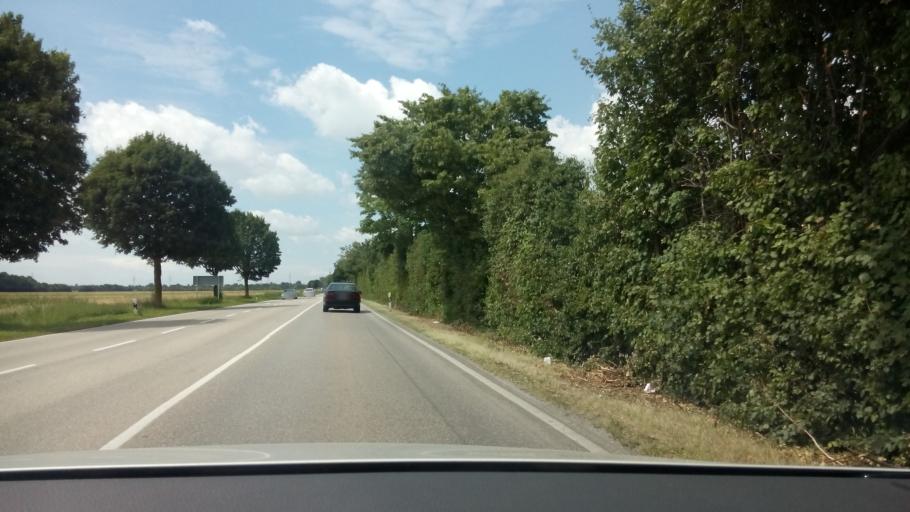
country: DE
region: Bavaria
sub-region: Upper Bavaria
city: Neufahrn bei Freising
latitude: 48.3077
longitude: 11.6479
